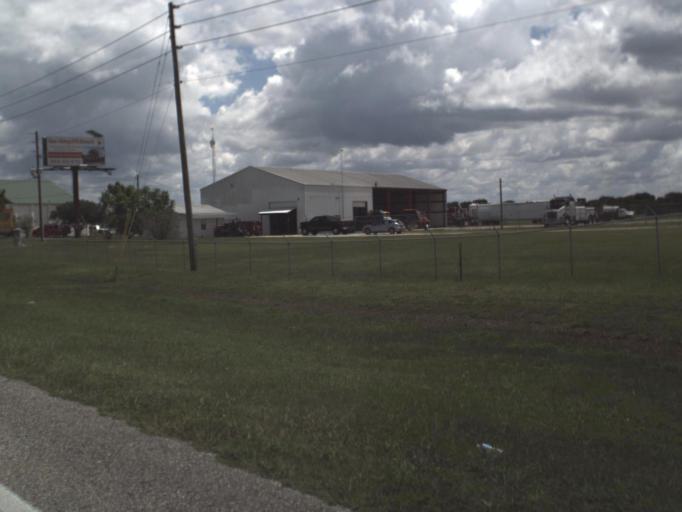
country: US
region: Florida
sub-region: Polk County
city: Babson Park
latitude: 27.8926
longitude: -81.4807
